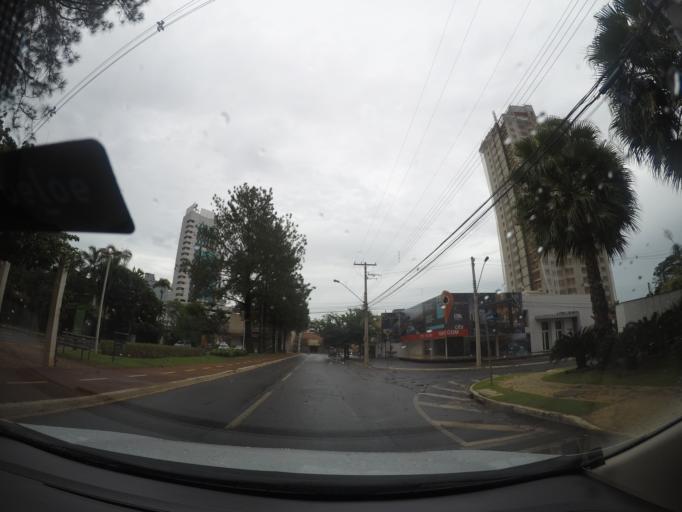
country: BR
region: Goias
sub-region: Goiania
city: Goiania
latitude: -16.6992
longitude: -49.2551
